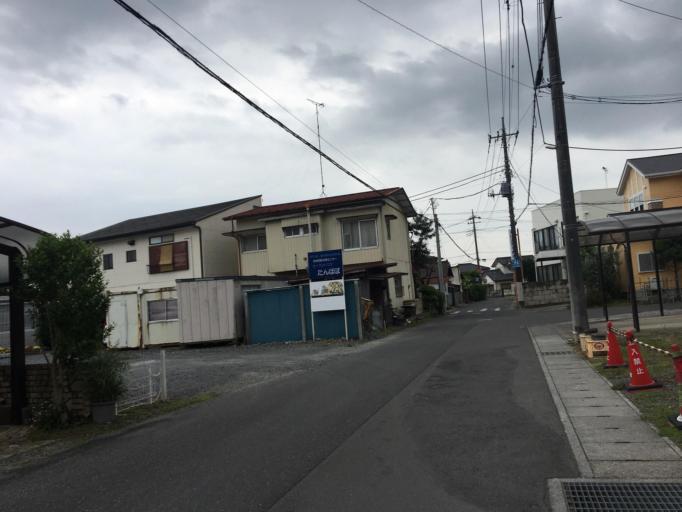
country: JP
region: Tochigi
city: Tochigi
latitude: 36.3887
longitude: 139.7312
